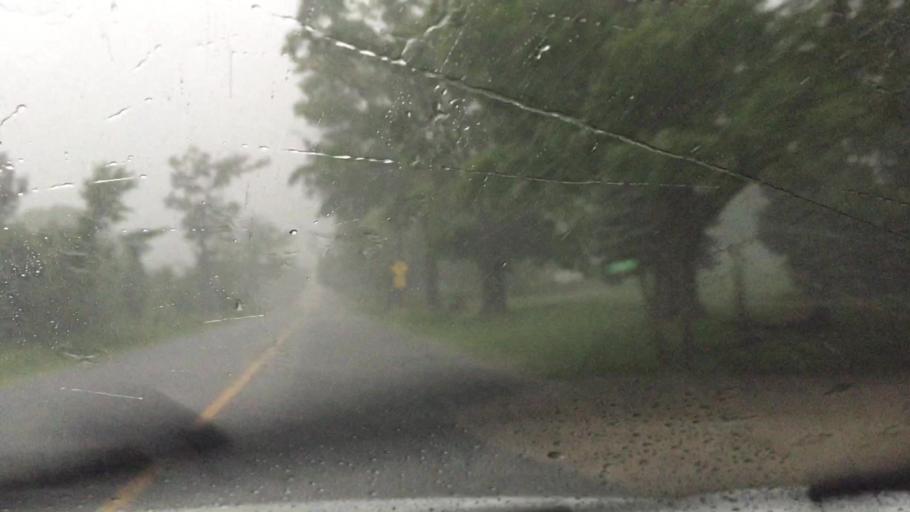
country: CA
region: Ontario
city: Markham
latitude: 43.8555
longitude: -79.2035
